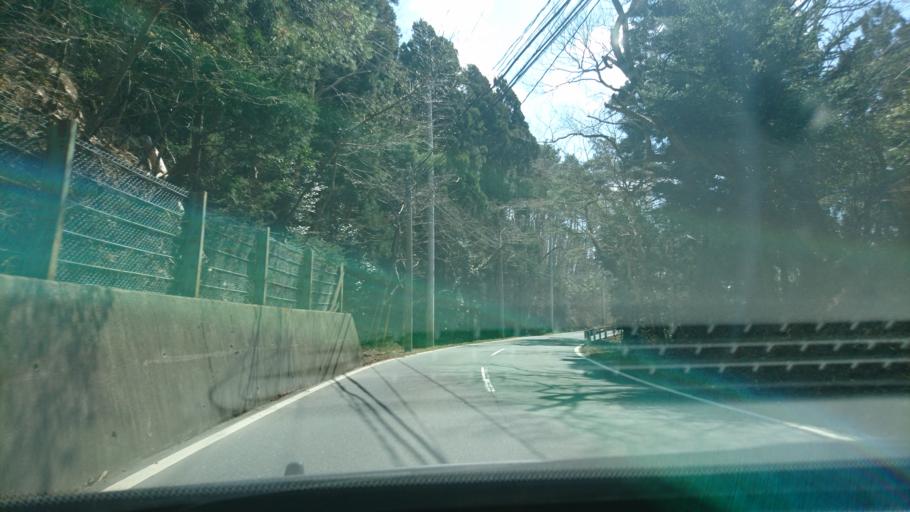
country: JP
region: Miyagi
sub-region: Oshika Gun
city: Onagawa Cho
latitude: 38.4416
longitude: 141.4808
